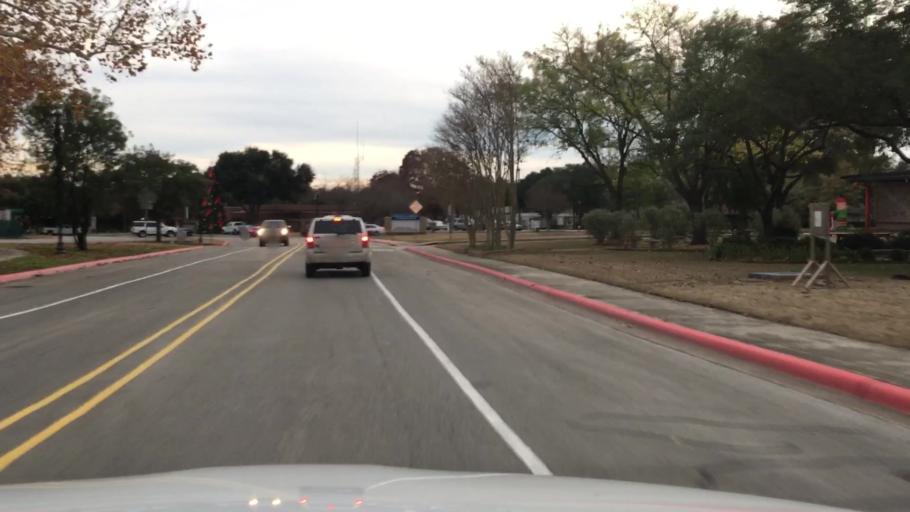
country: US
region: Texas
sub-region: Bexar County
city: Windcrest
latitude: 29.5183
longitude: -98.3817
